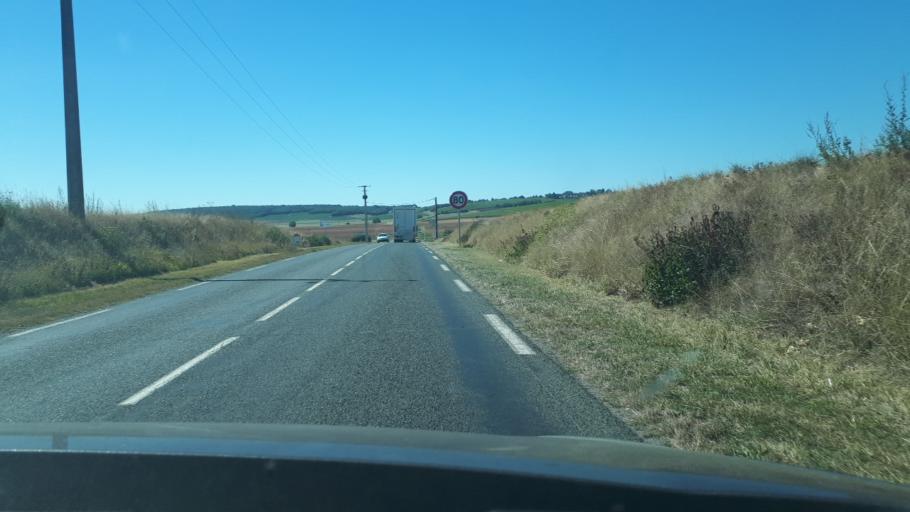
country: FR
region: Centre
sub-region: Departement du Cher
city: Sancerre
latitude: 47.2974
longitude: 2.7867
